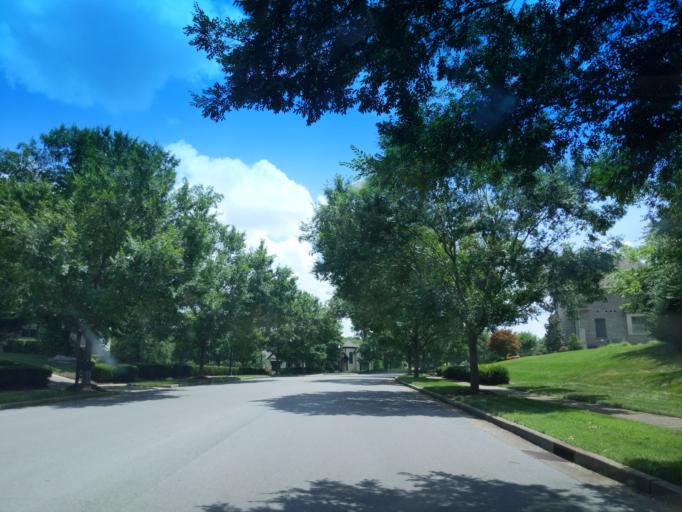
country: US
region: Tennessee
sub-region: Williamson County
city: Brentwood Estates
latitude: 36.0312
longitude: -86.7686
